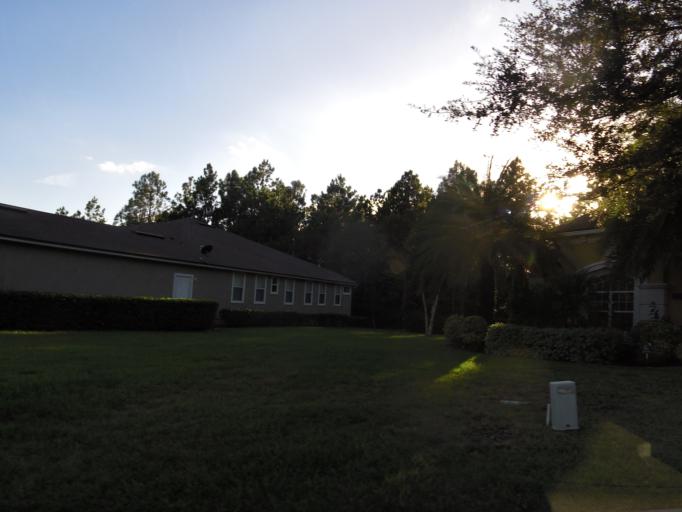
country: US
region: Florida
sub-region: Saint Johns County
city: Fruit Cove
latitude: 30.0636
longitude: -81.6414
